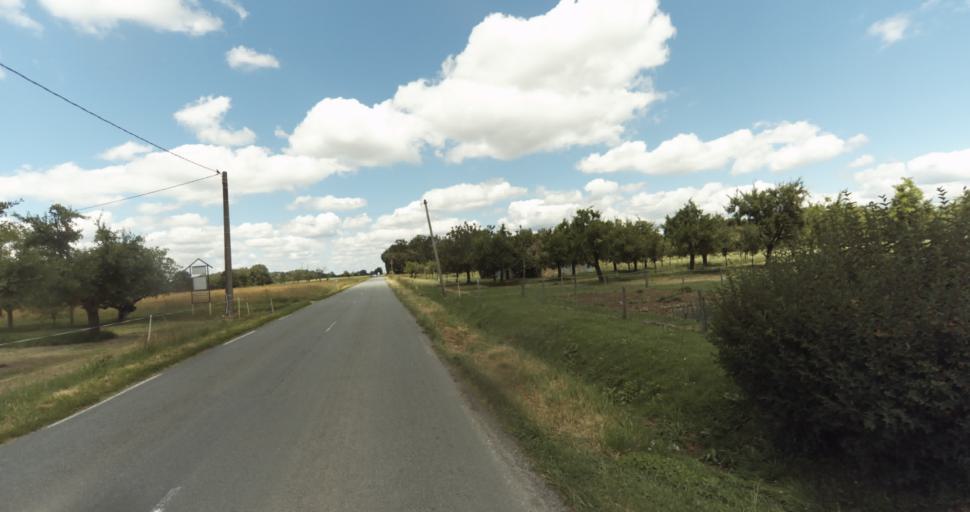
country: FR
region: Aquitaine
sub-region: Departement de la Dordogne
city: Beaumont-du-Perigord
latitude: 44.7417
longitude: 0.7815
